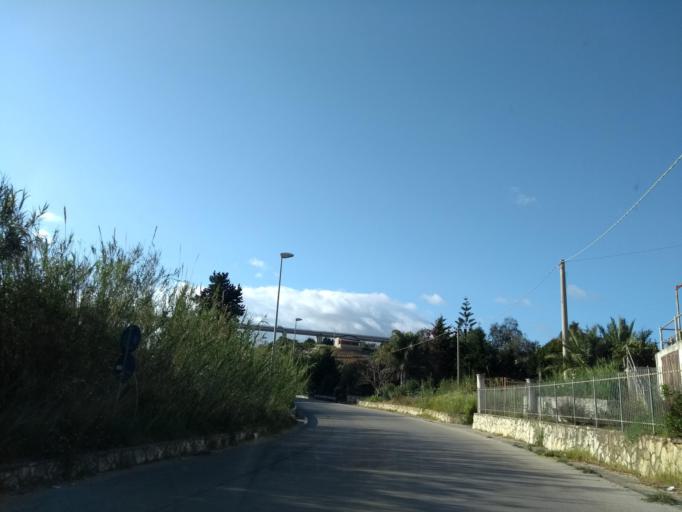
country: IT
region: Sicily
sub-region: Trapani
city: Alcamo
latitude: 38.0188
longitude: 12.9504
